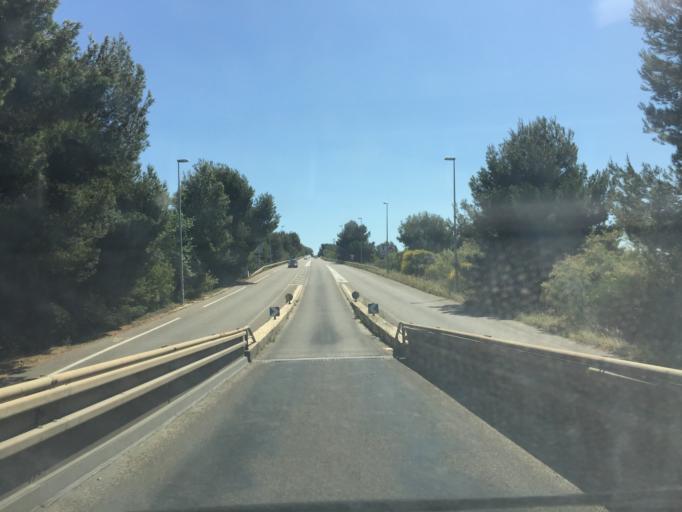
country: FR
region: Provence-Alpes-Cote d'Azur
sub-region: Departement des Bouches-du-Rhone
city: Vitrolles
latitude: 43.4589
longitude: 5.2334
